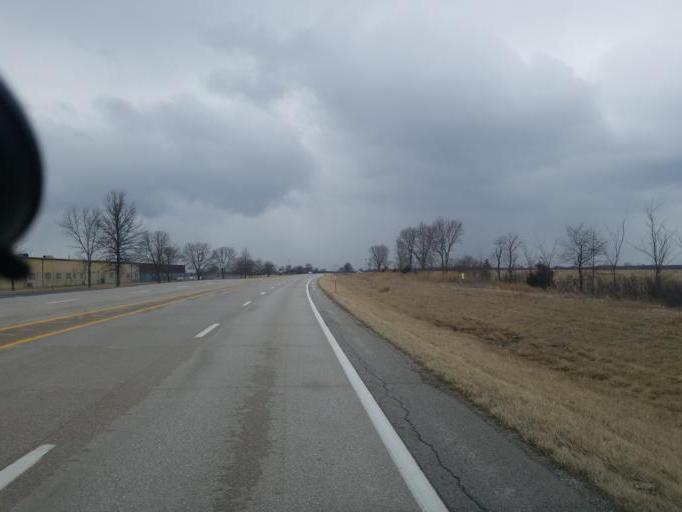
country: US
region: Missouri
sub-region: Macon County
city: Macon
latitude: 39.7984
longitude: -92.4756
